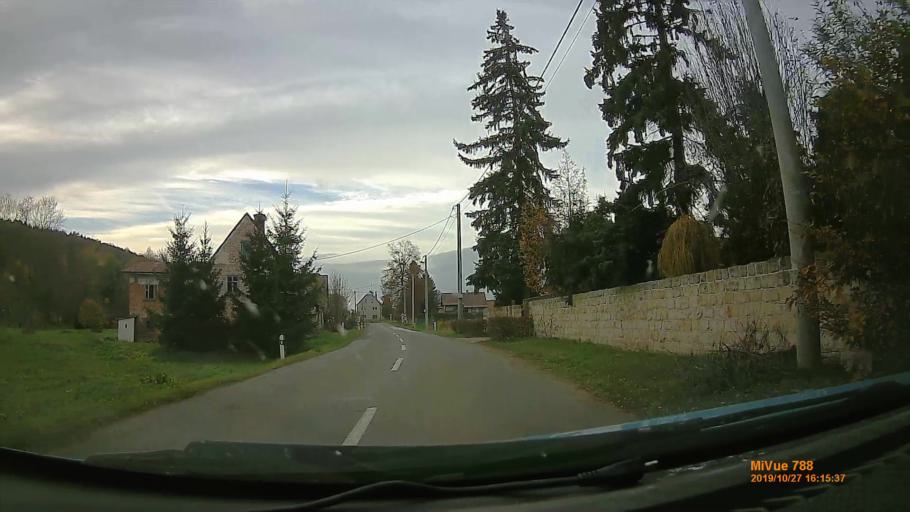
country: CZ
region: Kralovehradecky
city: Broumov
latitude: 50.5589
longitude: 16.3821
